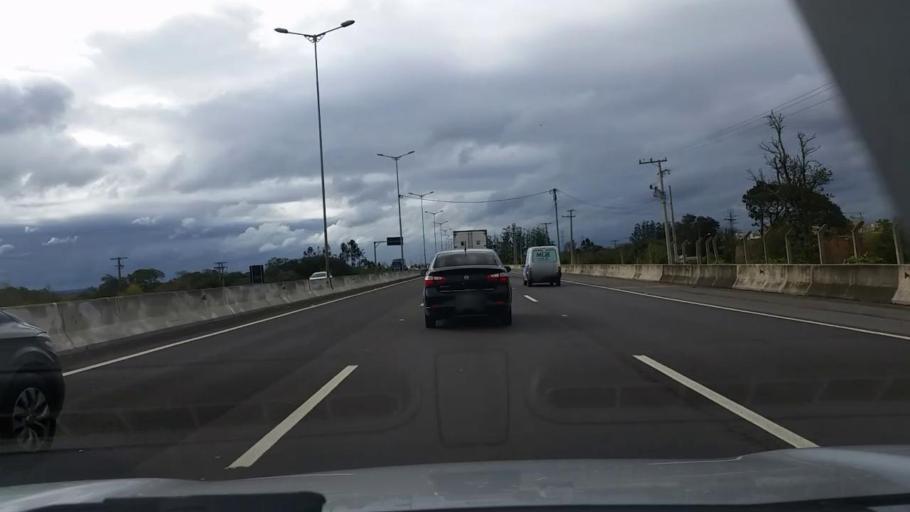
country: BR
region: Rio Grande do Sul
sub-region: Canoas
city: Canoas
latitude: -29.9618
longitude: -51.2027
